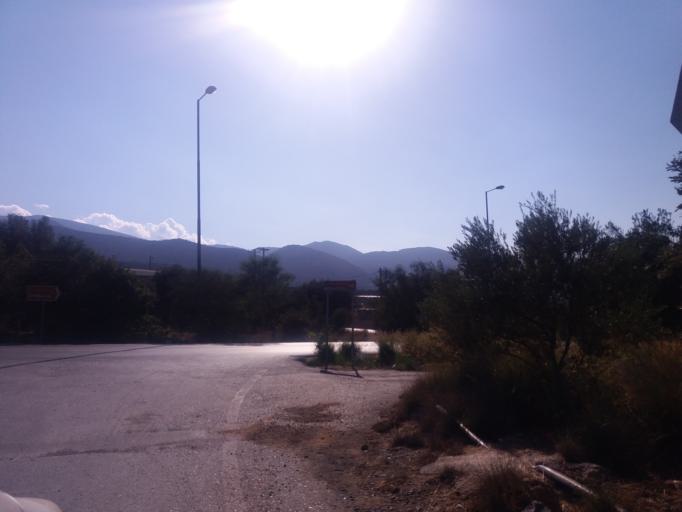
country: GR
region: Crete
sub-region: Nomos Irakleiou
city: Malia
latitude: 35.2901
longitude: 25.4908
